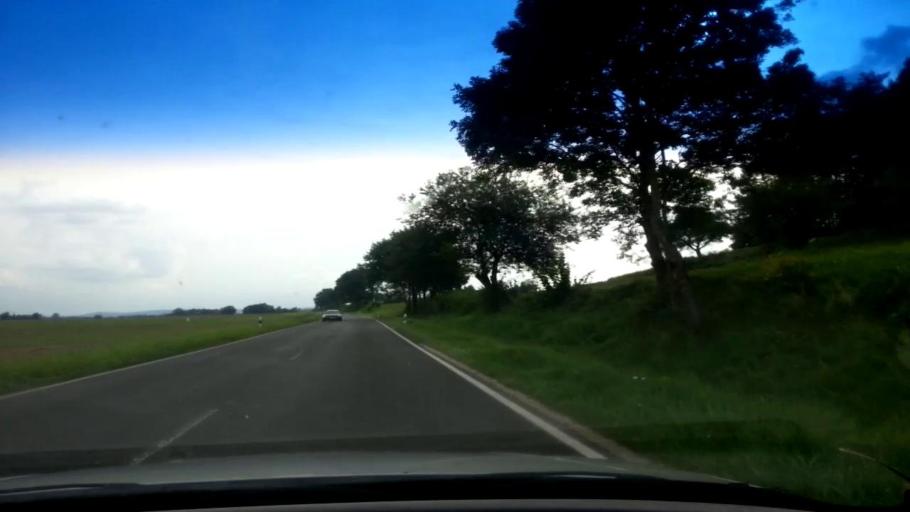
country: DE
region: Bavaria
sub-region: Upper Franconia
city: Zapfendorf
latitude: 50.0422
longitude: 10.9217
